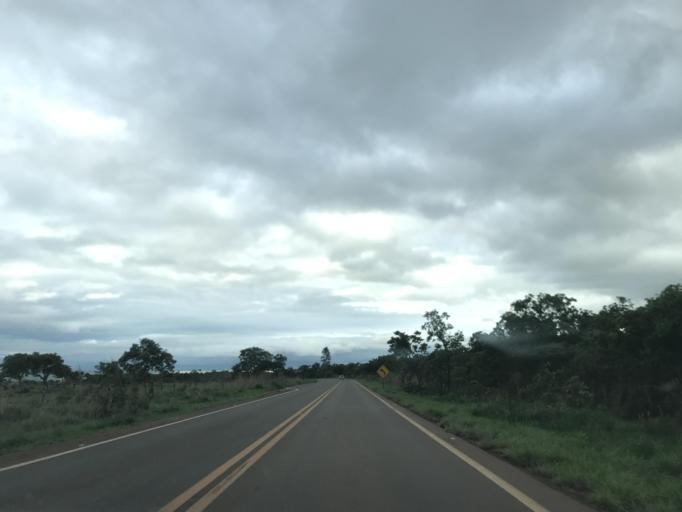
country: BR
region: Goias
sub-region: Luziania
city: Luziania
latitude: -16.4086
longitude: -48.1177
